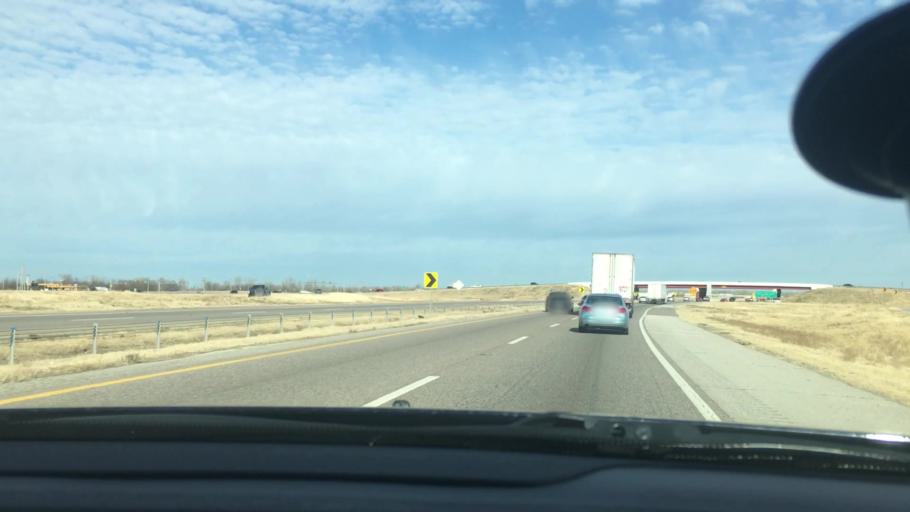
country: US
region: Oklahoma
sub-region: McClain County
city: Goldsby
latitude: 35.1774
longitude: -97.4943
